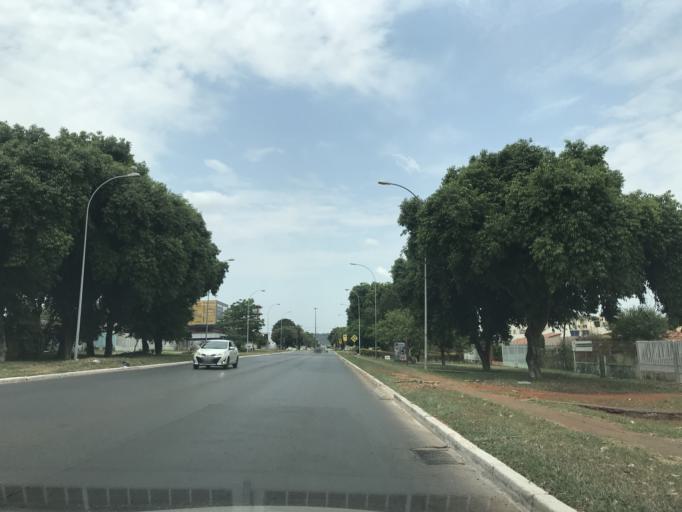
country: BR
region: Federal District
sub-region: Brasilia
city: Brasilia
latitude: -15.6546
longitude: -47.8047
